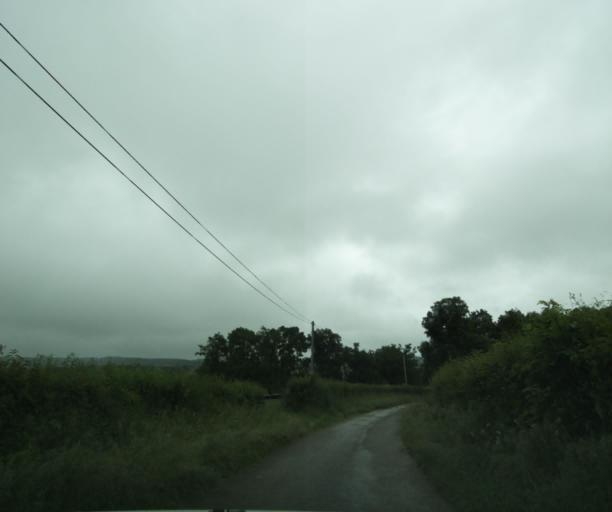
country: FR
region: Bourgogne
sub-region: Departement de Saone-et-Loire
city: La Clayette
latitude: 46.3516
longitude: 4.2300
